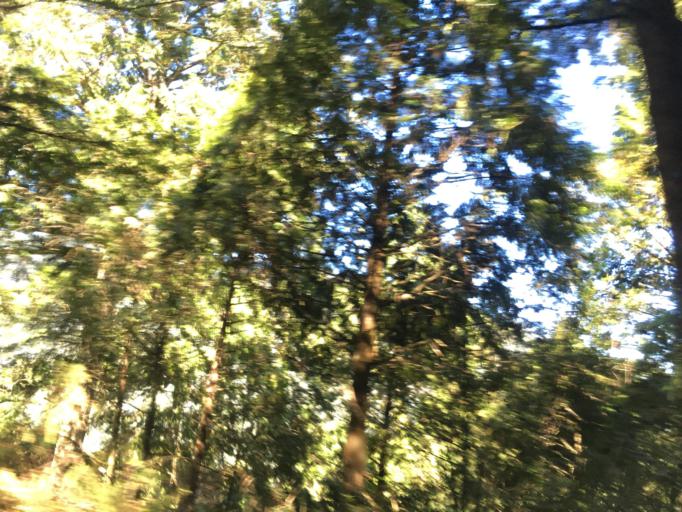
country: TW
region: Taiwan
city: Daxi
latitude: 24.6030
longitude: 121.4538
